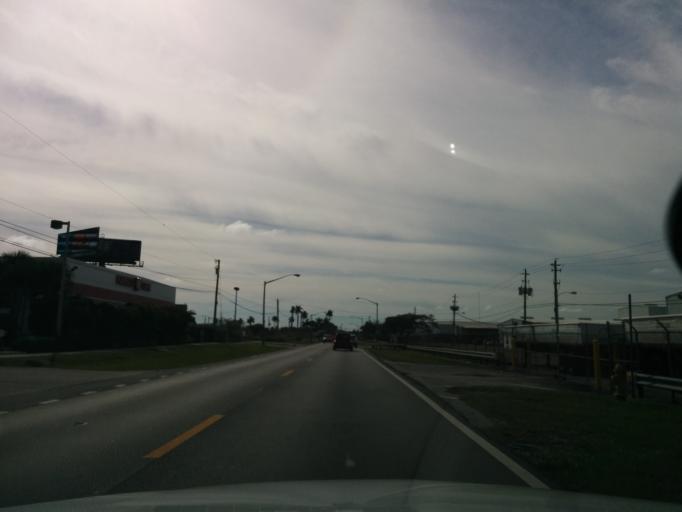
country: US
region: Florida
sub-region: Miami-Dade County
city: Florida City
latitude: 25.4549
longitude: -80.4773
